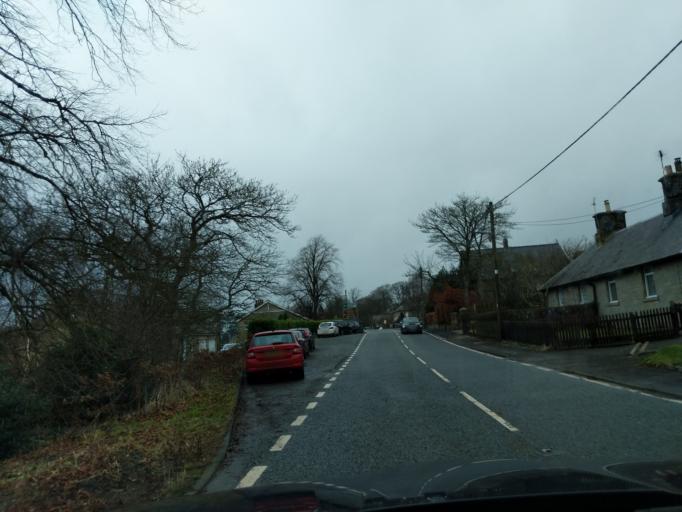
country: GB
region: England
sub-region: Northumberland
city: Otterburn
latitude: 55.2306
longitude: -2.1741
